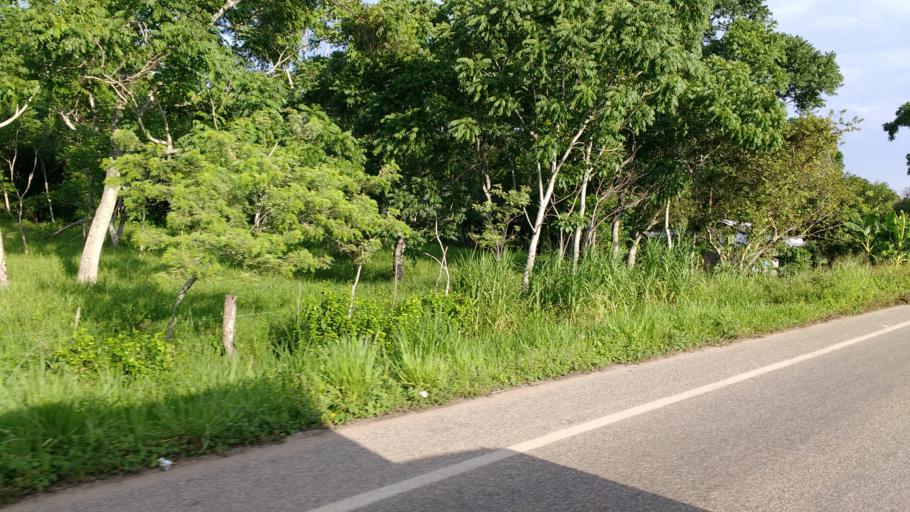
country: MX
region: Tabasco
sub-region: Teapa
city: Eureka y Belen
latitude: 17.6258
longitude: -92.9628
